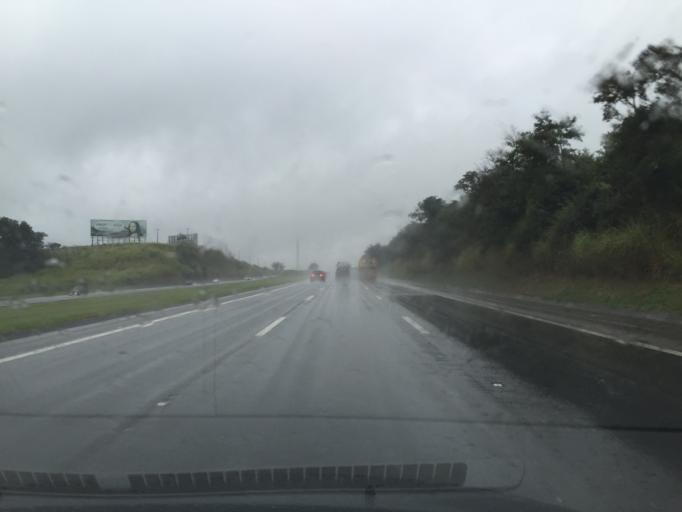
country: BR
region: Sao Paulo
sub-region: Itu
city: Itu
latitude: -23.4038
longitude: -47.3189
